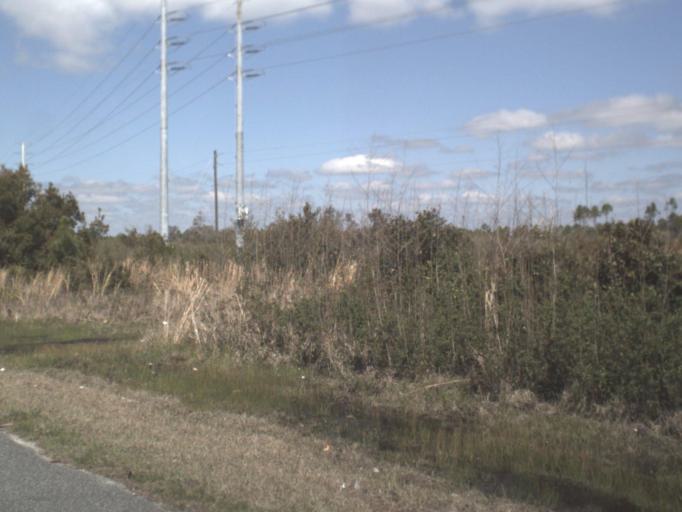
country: US
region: Florida
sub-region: Franklin County
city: Apalachicola
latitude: 29.7204
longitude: -85.0676
